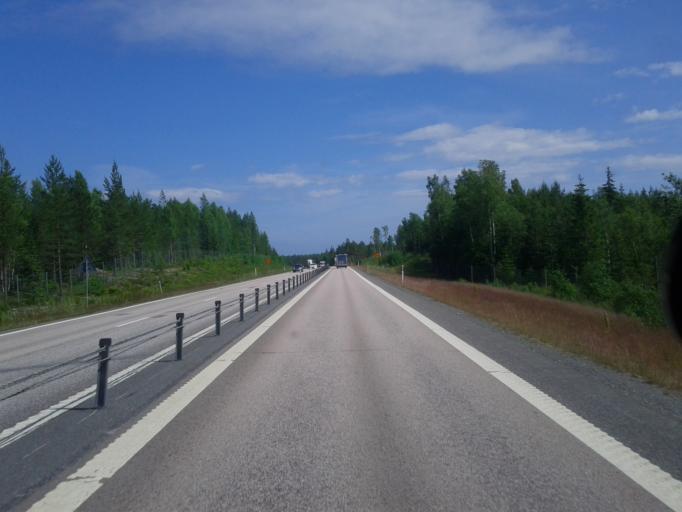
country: SE
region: Vaesternorrland
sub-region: OErnskoeldsviks Kommun
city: Husum
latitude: 63.4575
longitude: 19.2475
